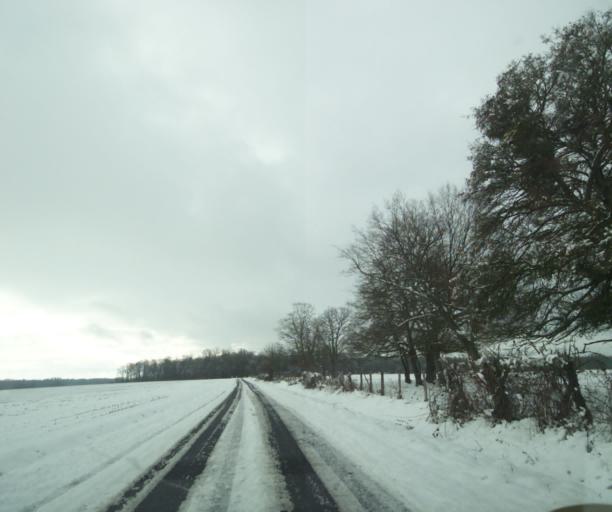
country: FR
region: Champagne-Ardenne
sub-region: Departement de la Haute-Marne
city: Montier-en-Der
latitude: 48.4865
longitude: 4.6851
